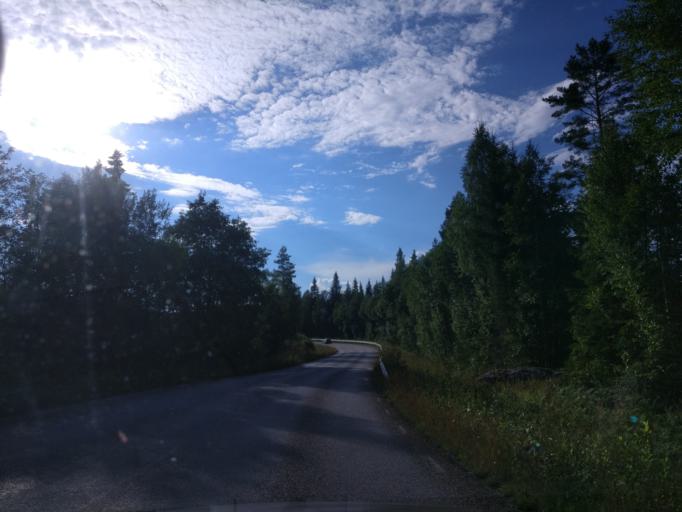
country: SE
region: Dalarna
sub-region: Ludvika Kommun
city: Ludvika
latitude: 60.2918
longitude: 15.1277
